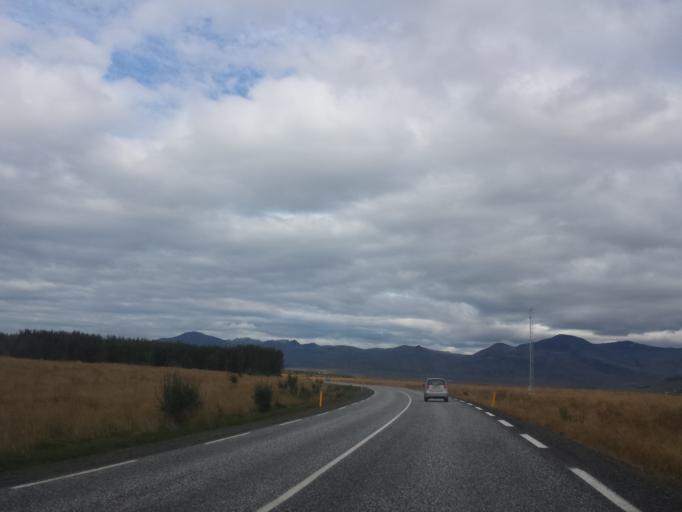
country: IS
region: West
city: Borgarnes
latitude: 64.3554
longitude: -21.8061
